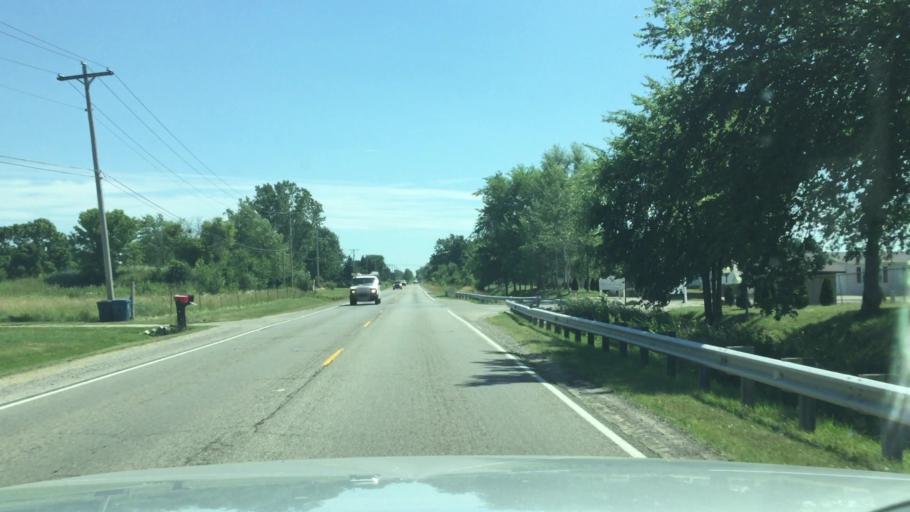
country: US
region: Michigan
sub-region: Genesee County
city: Swartz Creek
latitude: 42.9552
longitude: -83.8111
